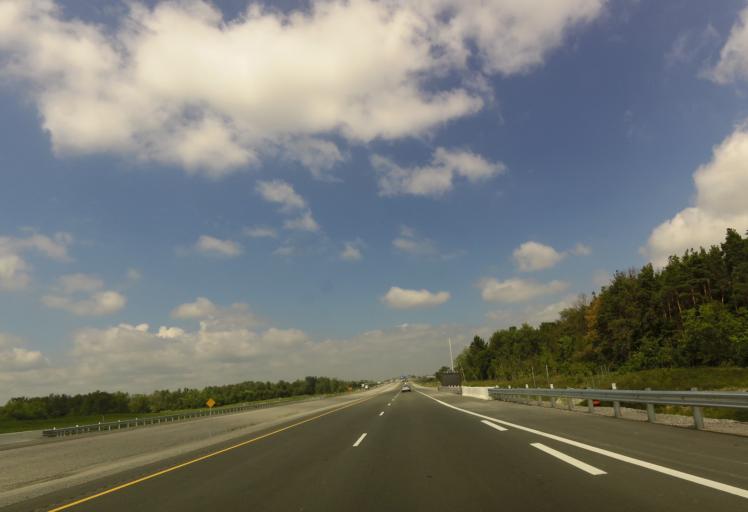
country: CA
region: Ontario
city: Ajax
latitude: 43.9291
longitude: -79.0011
